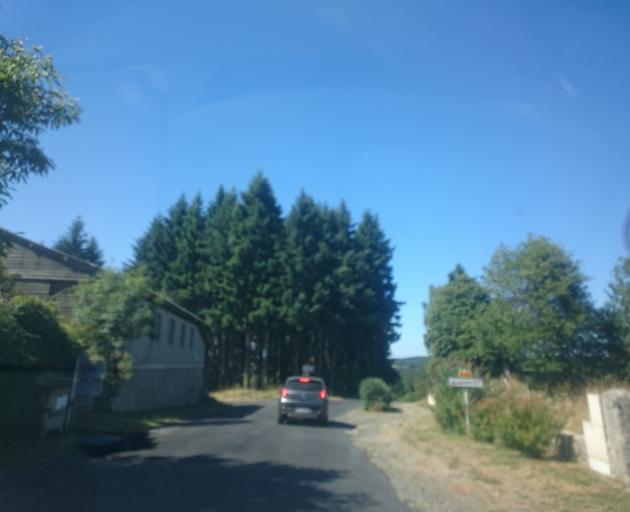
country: FR
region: Auvergne
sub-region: Departement du Cantal
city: Saint-Mamet-la-Salvetat
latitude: 44.7849
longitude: 2.3538
